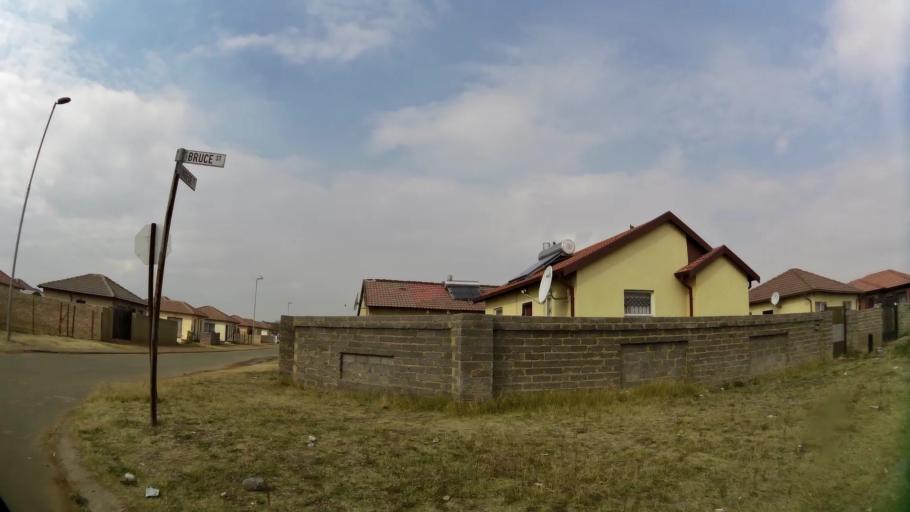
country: ZA
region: Gauteng
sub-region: Sedibeng District Municipality
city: Vanderbijlpark
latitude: -26.6833
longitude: 27.8432
